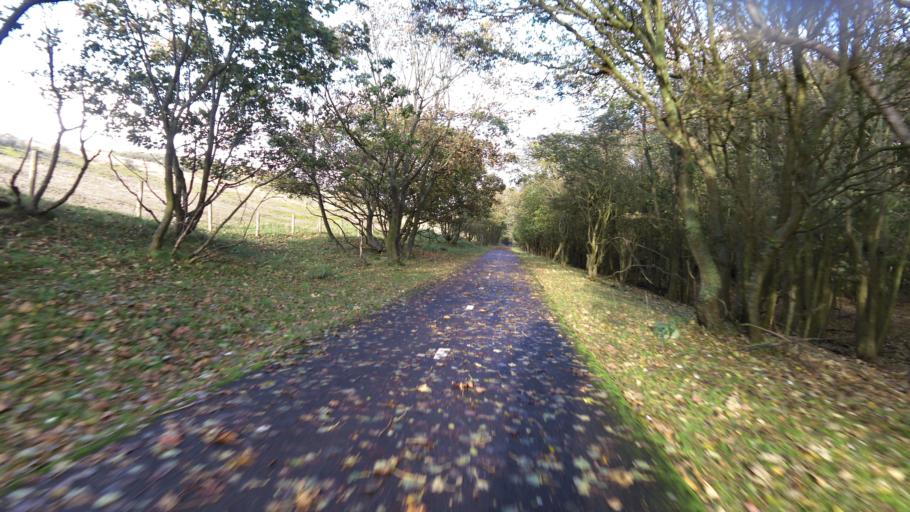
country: NL
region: South Holland
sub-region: Gemeente Noordwijkerhout
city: Noordwijkerhout
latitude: 52.2928
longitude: 4.4914
